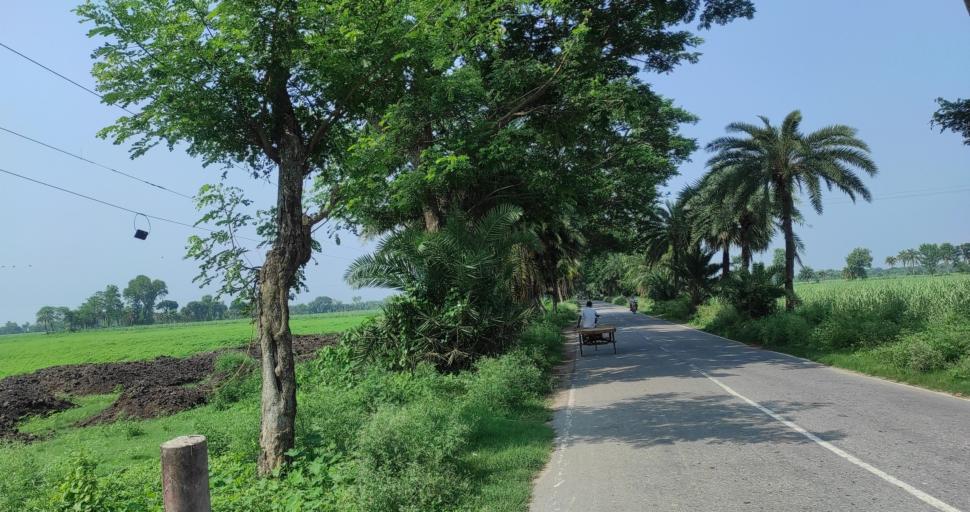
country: BD
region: Rajshahi
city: Ishurdi
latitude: 24.2704
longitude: 89.0544
